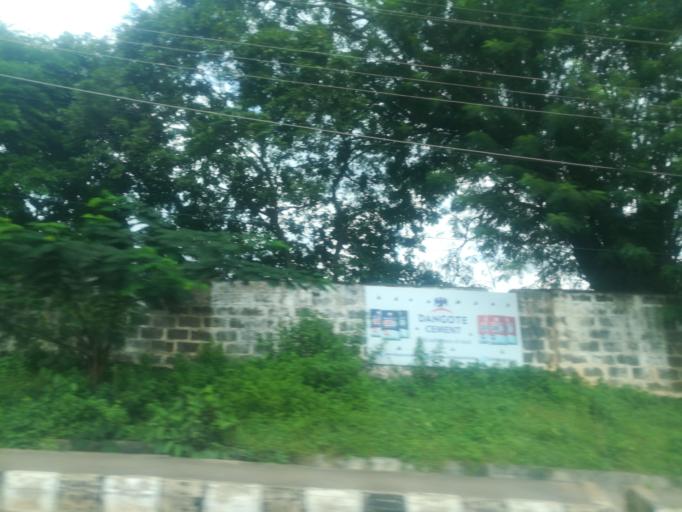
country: NG
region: Oyo
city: Ibadan
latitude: 7.4040
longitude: 3.8708
